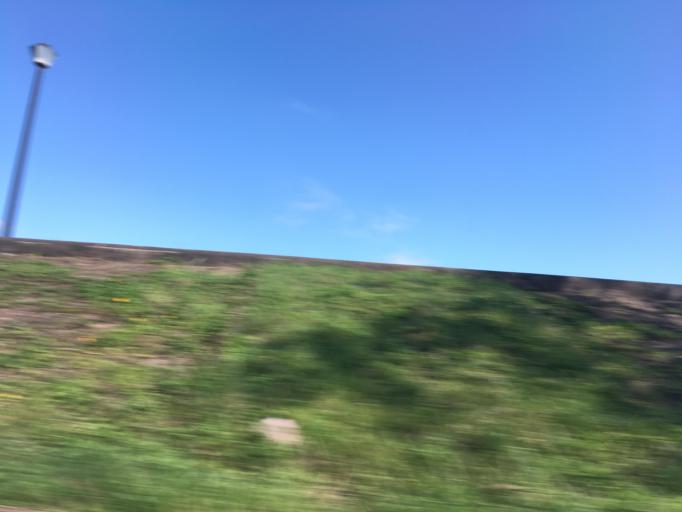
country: TW
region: Taiwan
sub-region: Yilan
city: Yilan
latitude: 24.7580
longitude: 121.7374
